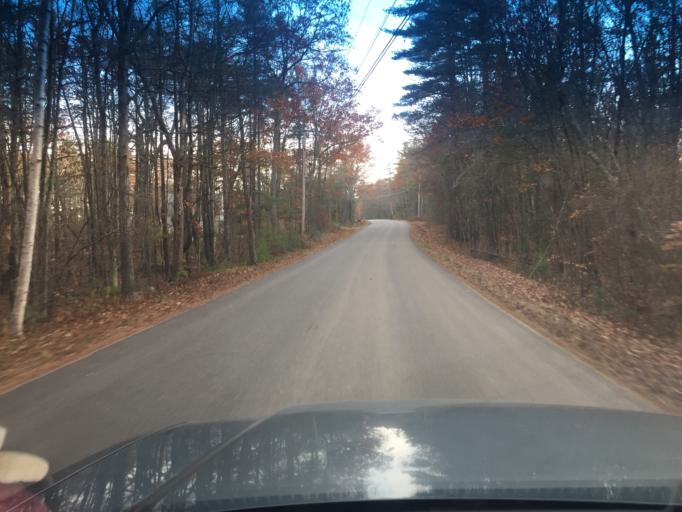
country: US
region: Maine
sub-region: York County
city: Eliot
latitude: 43.1946
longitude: -70.7482
